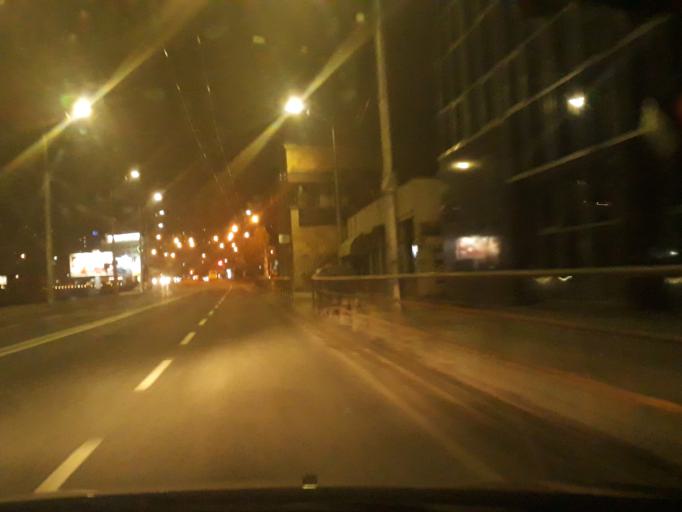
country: BA
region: Federation of Bosnia and Herzegovina
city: Kobilja Glava
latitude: 43.8540
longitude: 18.4106
